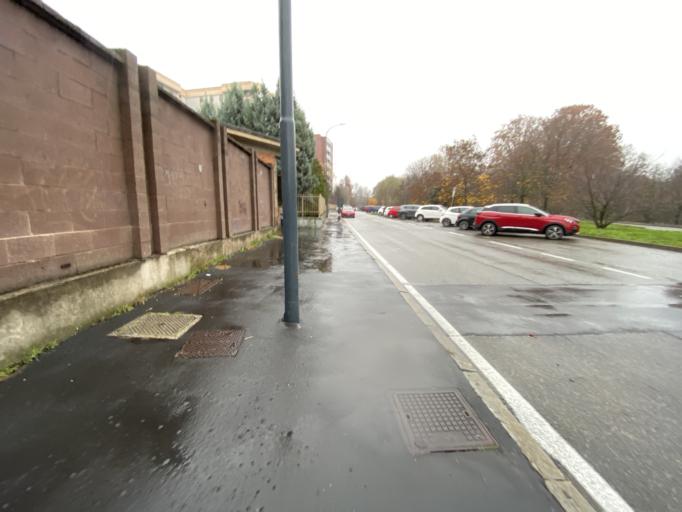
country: IT
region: Lombardy
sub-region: Citta metropolitana di Milano
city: Romano Banco
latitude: 45.4414
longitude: 9.1132
